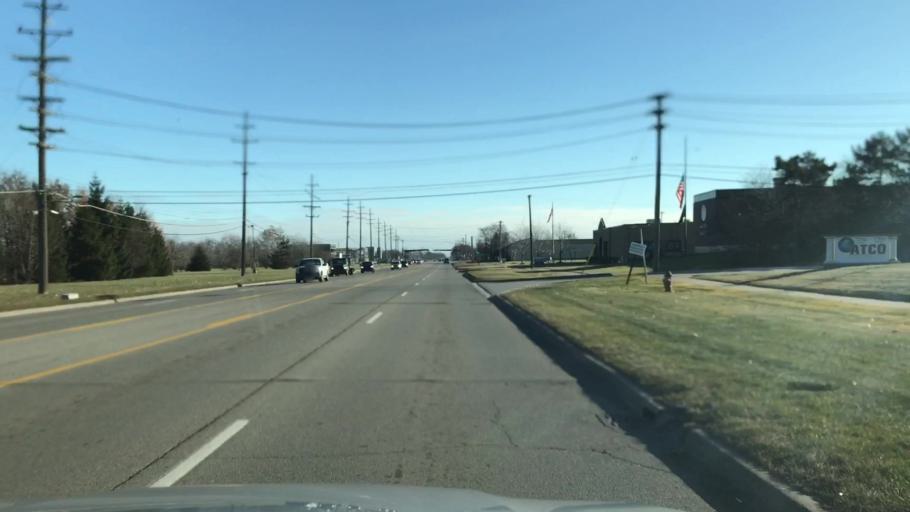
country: US
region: Michigan
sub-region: Macomb County
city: Sterling Heights
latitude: 42.5510
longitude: -83.0346
